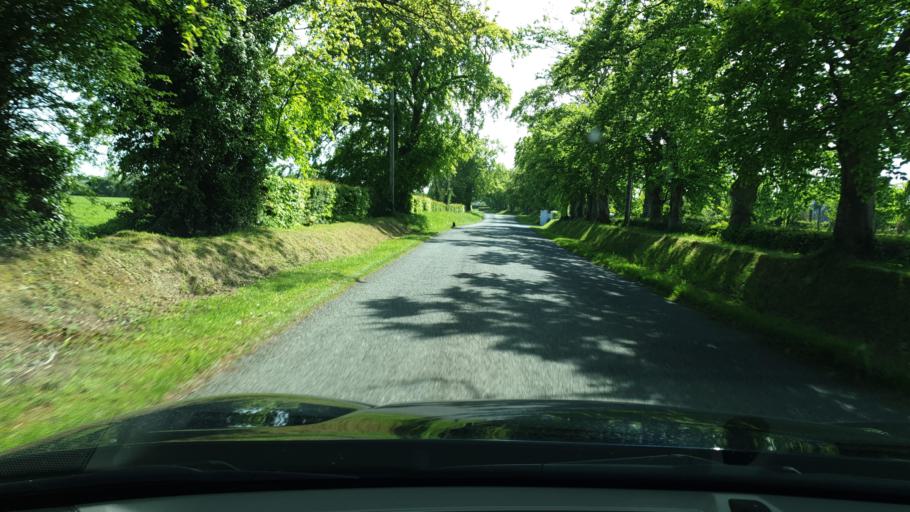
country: IE
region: Leinster
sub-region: Kildare
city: Maynooth
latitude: 53.4361
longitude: -6.5640
